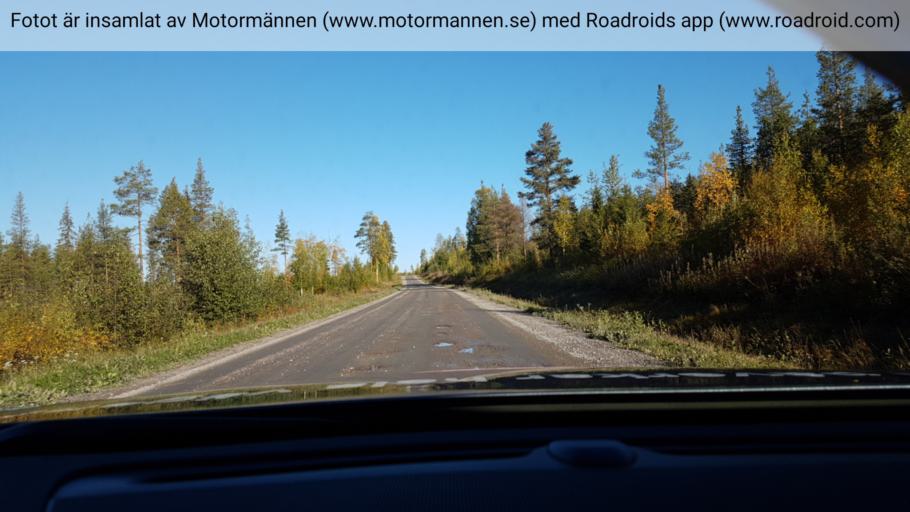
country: SE
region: Norrbotten
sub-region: Alvsbyns Kommun
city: AElvsbyn
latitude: 66.2134
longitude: 21.1699
